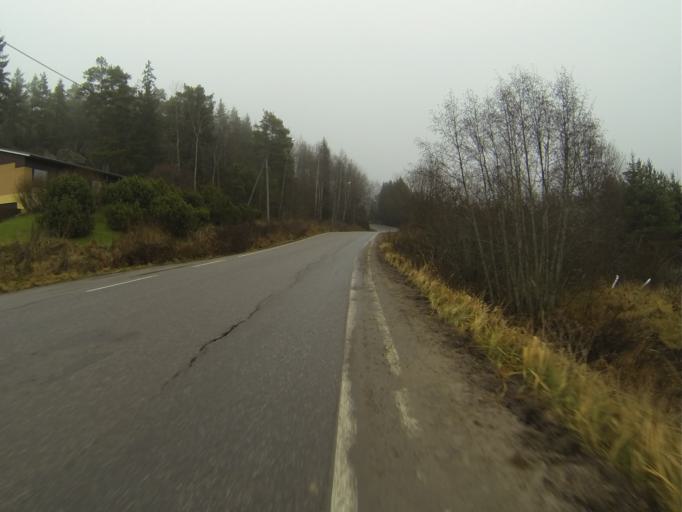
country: FI
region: Varsinais-Suomi
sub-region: Salo
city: Halikko
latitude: 60.4167
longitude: 22.9175
